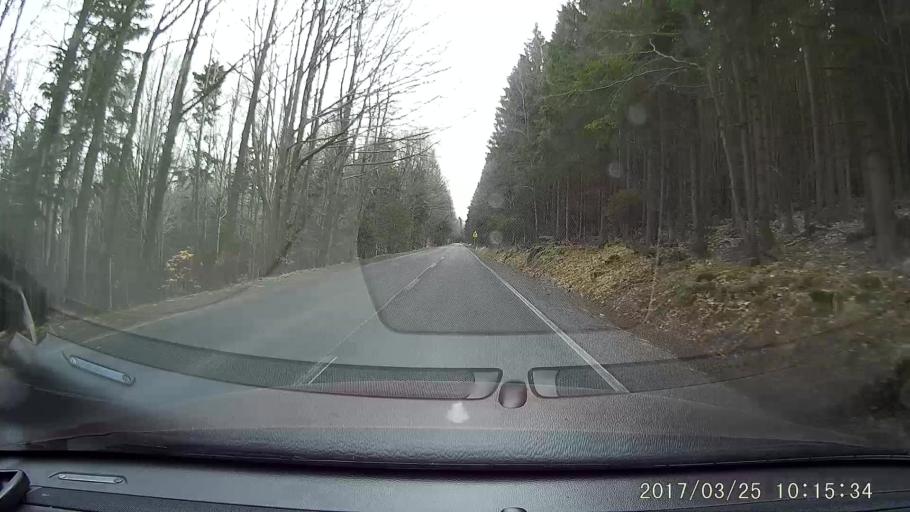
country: PL
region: Lower Silesian Voivodeship
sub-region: Powiat jeleniogorski
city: Szklarska Poreba
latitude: 50.8510
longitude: 15.5100
